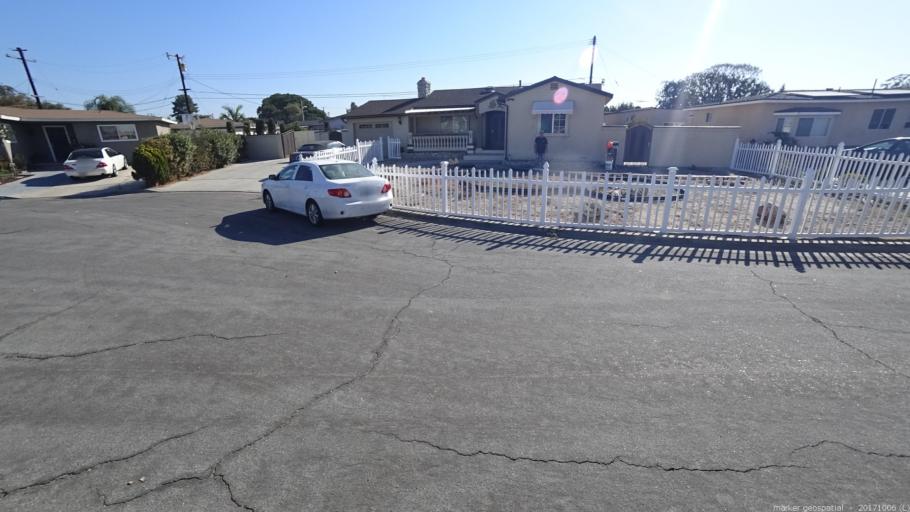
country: US
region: California
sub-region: Orange County
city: Stanton
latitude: 33.7831
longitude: -117.9730
